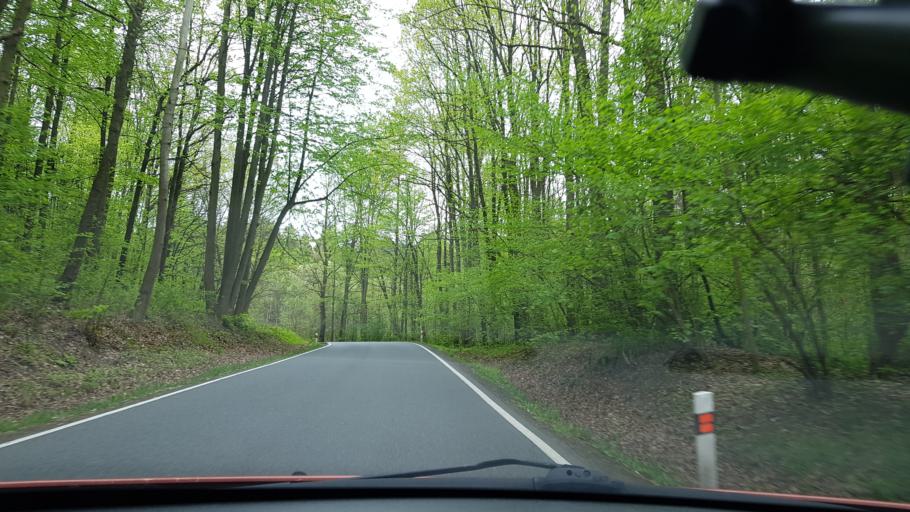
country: CZ
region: Olomoucky
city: Vidnava
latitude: 50.3677
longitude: 17.1935
